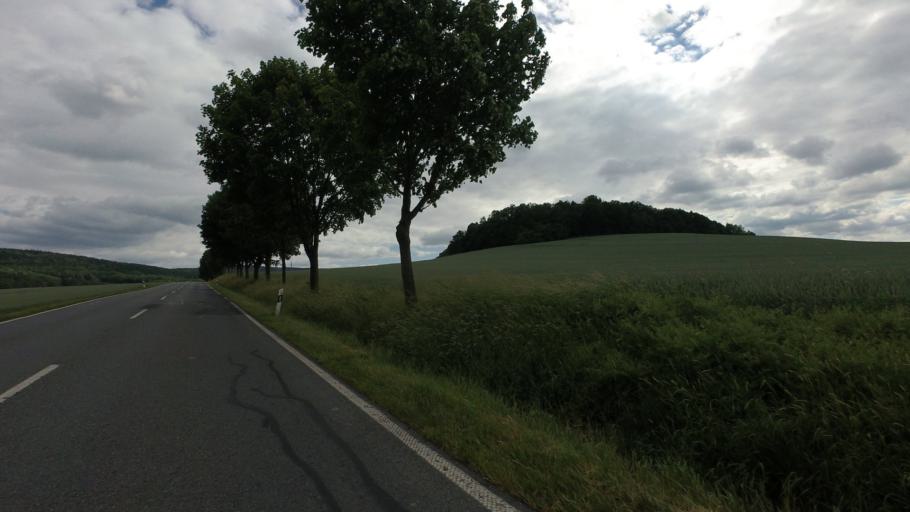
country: DE
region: Saxony
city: Neustadt in Sachsen
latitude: 51.0203
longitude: 14.2324
